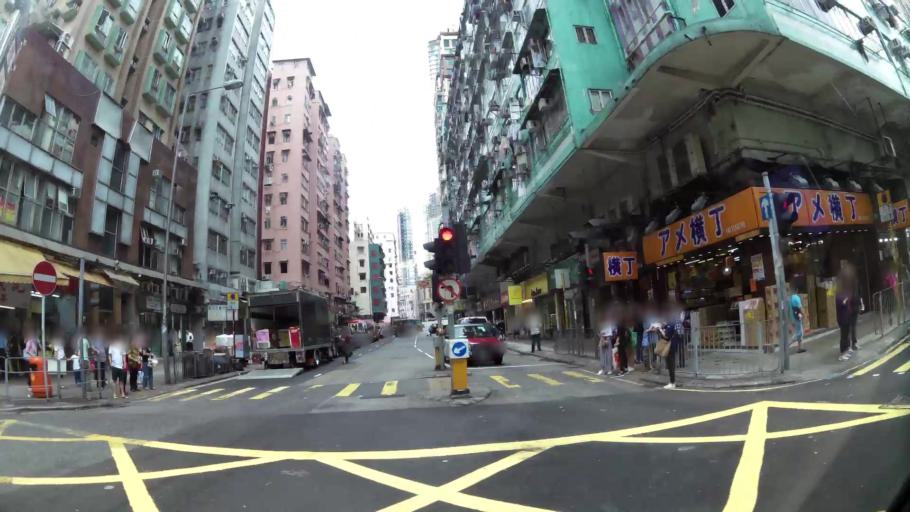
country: HK
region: Kowloon City
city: Kowloon
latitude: 22.3226
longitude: 114.1885
